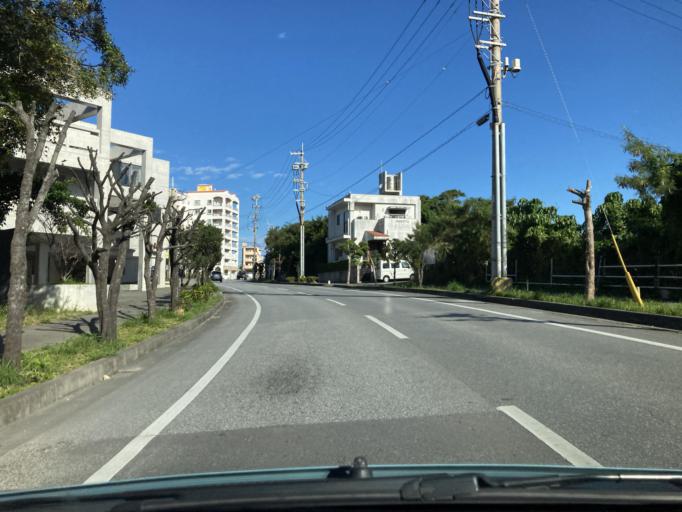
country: JP
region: Okinawa
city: Chatan
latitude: 26.3648
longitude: 127.7481
